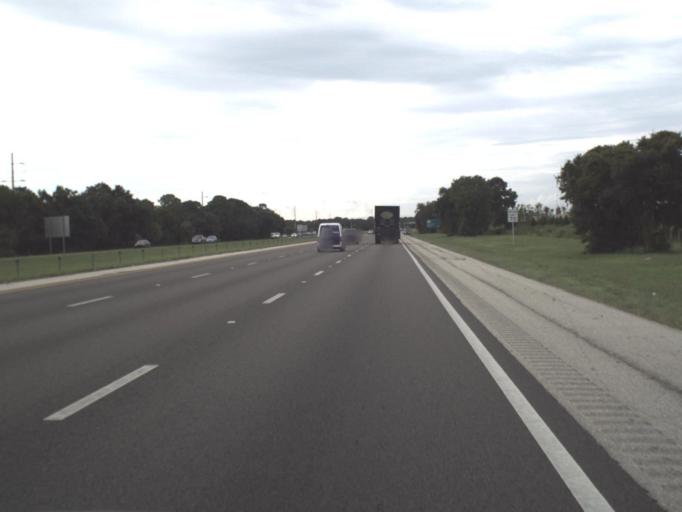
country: US
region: Florida
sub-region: Sarasota County
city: Lake Sarasota
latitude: 27.2588
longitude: -82.4494
